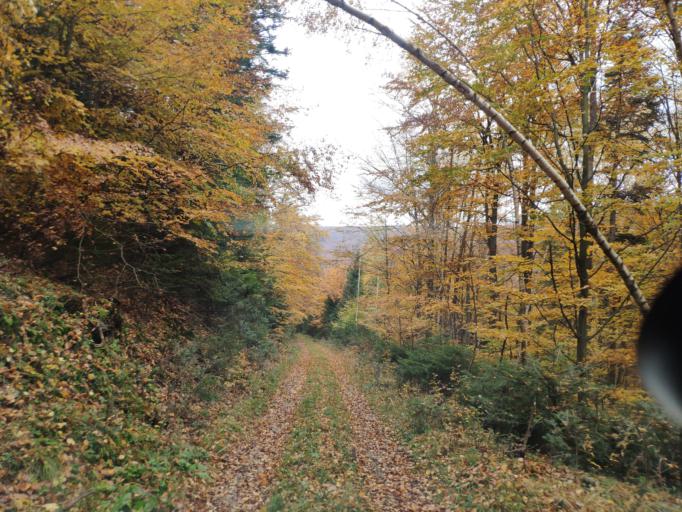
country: SK
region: Kosicky
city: Medzev
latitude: 48.7575
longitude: 20.9797
